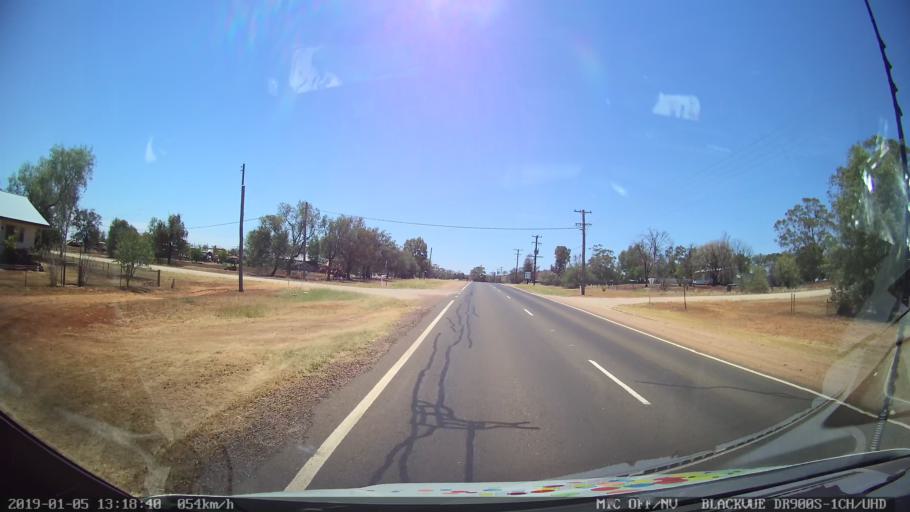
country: AU
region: New South Wales
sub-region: Gunnedah
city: Gunnedah
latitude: -31.0969
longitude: 149.9123
